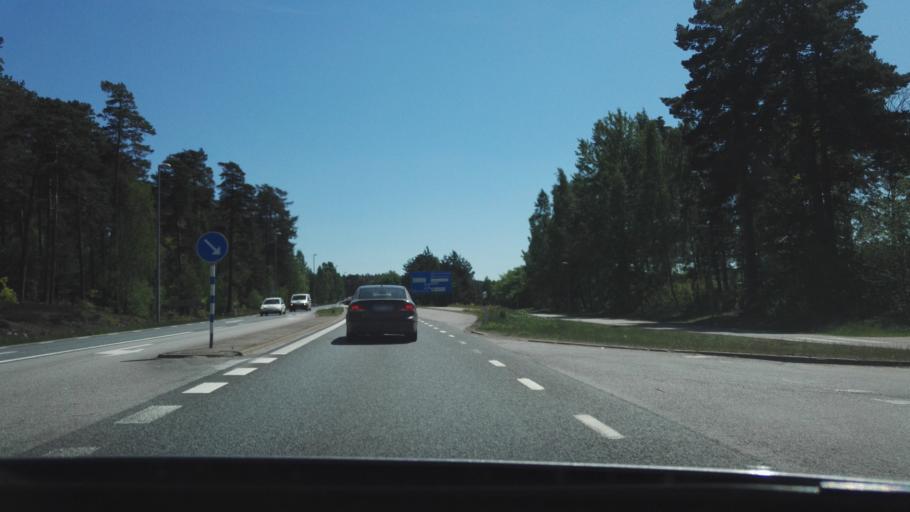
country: SE
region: Kronoberg
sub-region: Vaxjo Kommun
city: Vaexjoe
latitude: 56.8833
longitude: 14.8304
